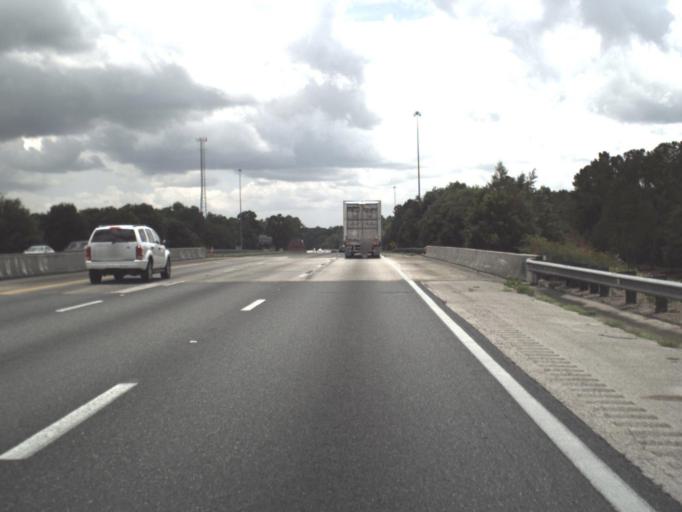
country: US
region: Florida
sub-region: Alachua County
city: Gainesville
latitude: 29.4974
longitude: -82.2952
